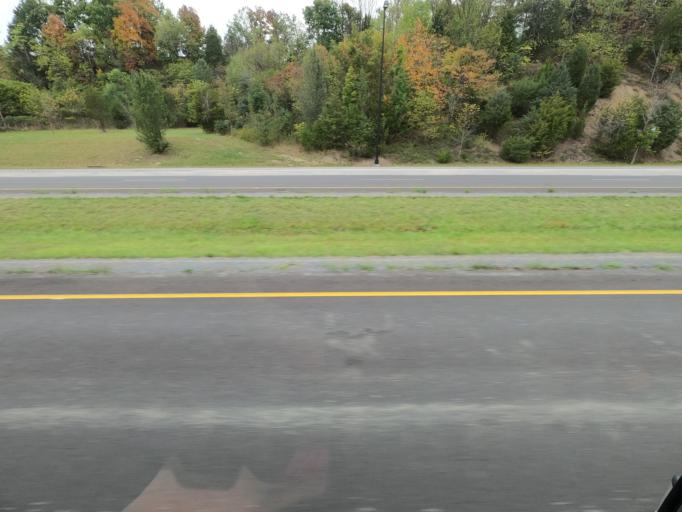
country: US
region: Tennessee
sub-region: Sullivan County
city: Kingsport
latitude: 36.5066
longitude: -82.5500
